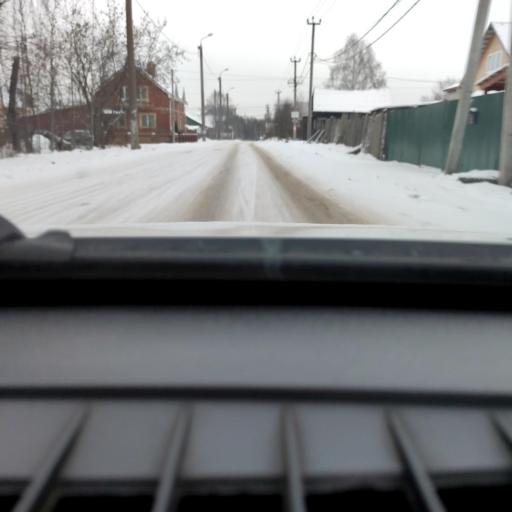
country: RU
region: Perm
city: Perm
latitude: 58.0993
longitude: 56.3677
